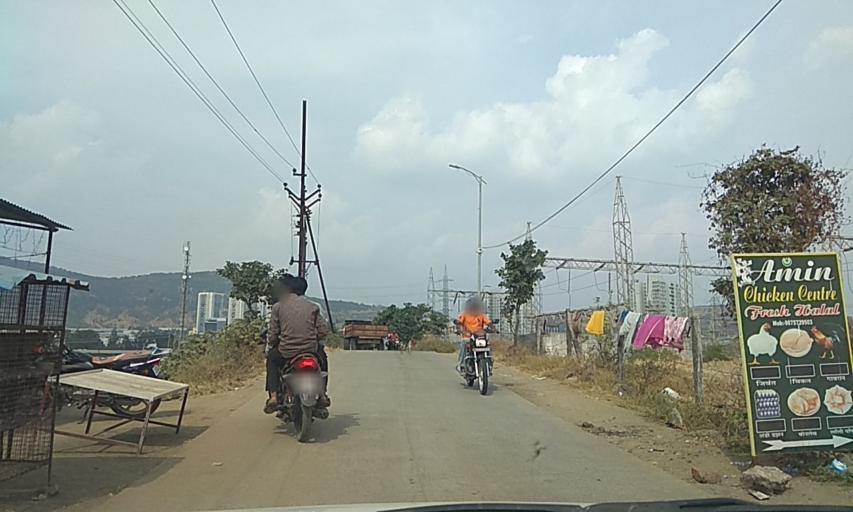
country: IN
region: Maharashtra
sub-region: Pune Division
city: Pimpri
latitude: 18.5867
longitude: 73.7059
